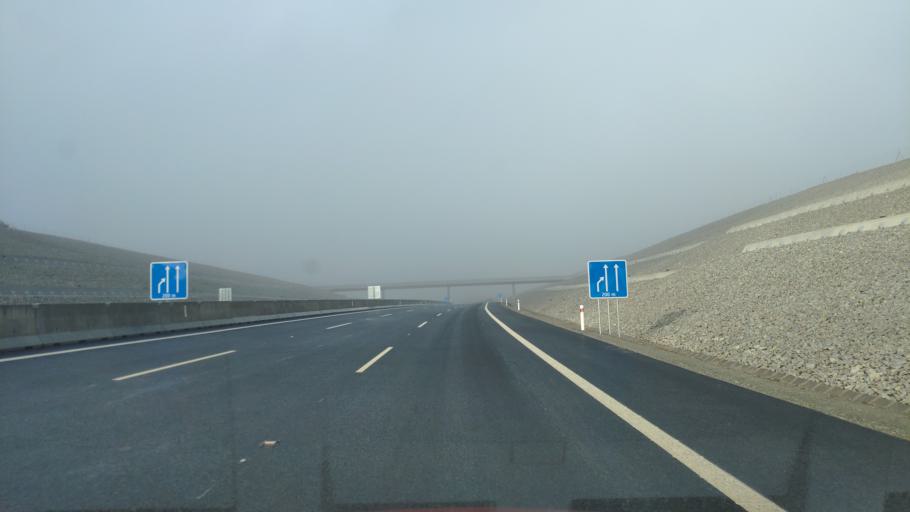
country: SK
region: Kosicky
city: Kosice
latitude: 48.7349
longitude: 21.3911
